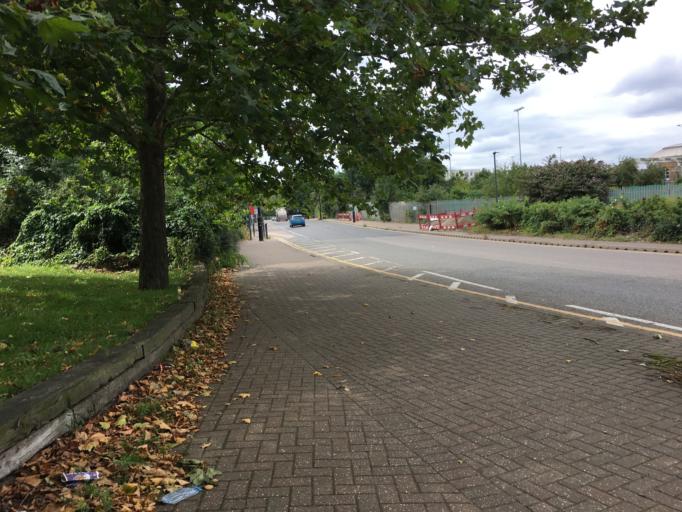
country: GB
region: England
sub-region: Greater London
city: East Ham
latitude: 51.5092
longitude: 0.0368
